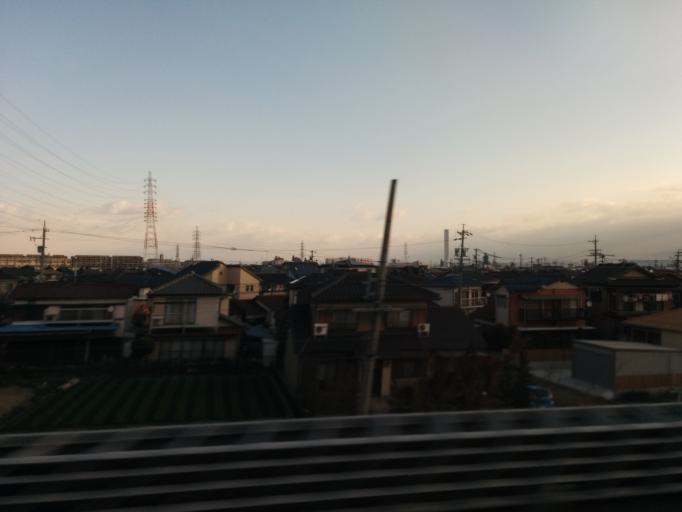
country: JP
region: Aichi
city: Inazawa
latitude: 35.2313
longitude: 136.7977
